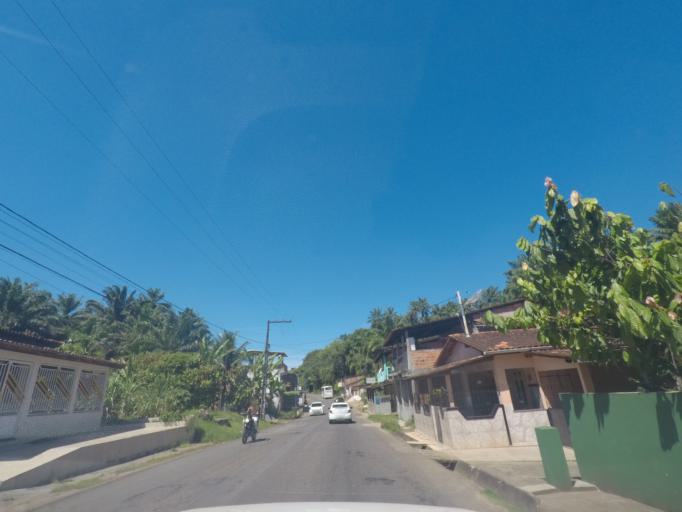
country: BR
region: Bahia
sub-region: Valenca
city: Valenca
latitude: -13.4379
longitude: -39.0795
